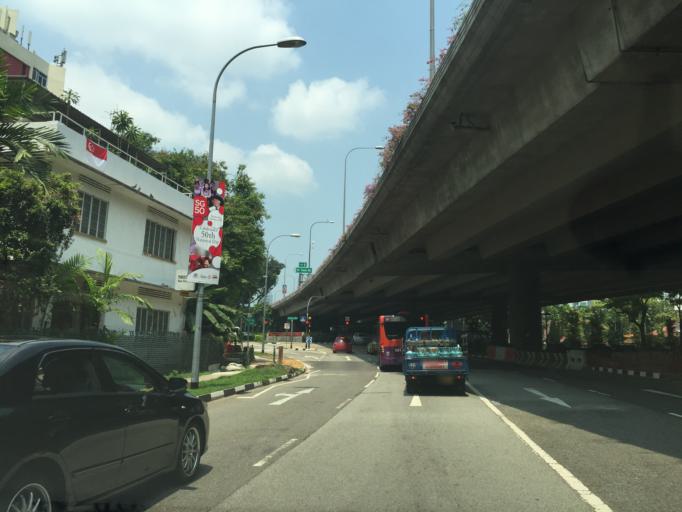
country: SG
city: Singapore
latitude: 1.3146
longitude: 103.8460
